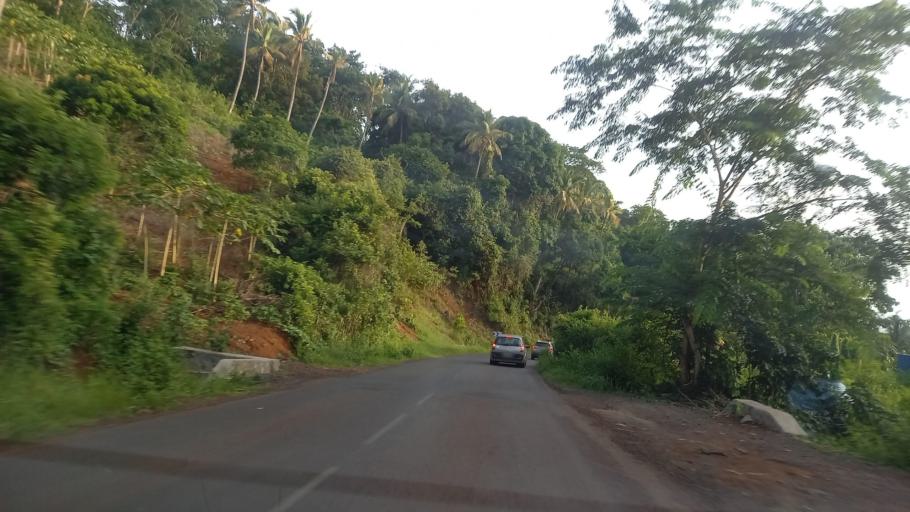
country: YT
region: M'Tsangamouji
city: M'Tsangamouji
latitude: -12.7538
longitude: 45.0905
